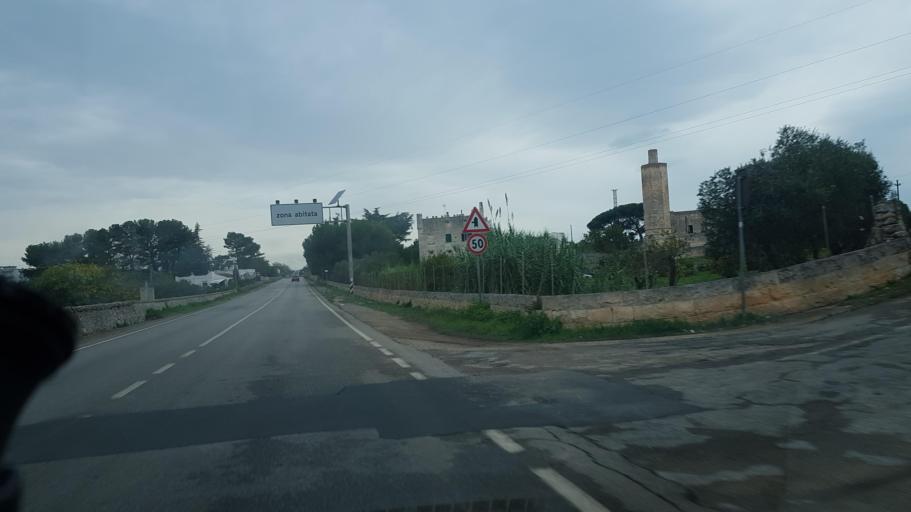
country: IT
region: Apulia
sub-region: Provincia di Brindisi
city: Ostuni
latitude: 40.7190
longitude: 17.6112
